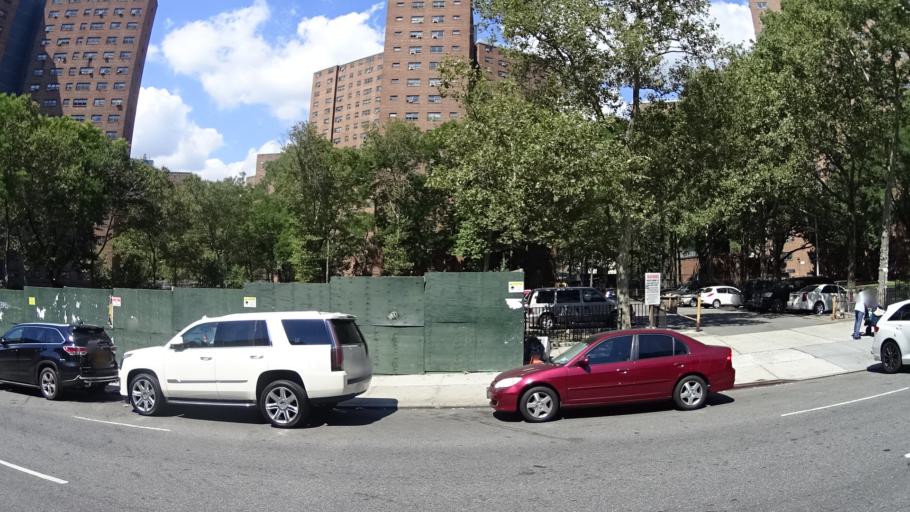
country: US
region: New Jersey
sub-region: Bergen County
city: Edgewater
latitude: 40.8166
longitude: -73.9539
